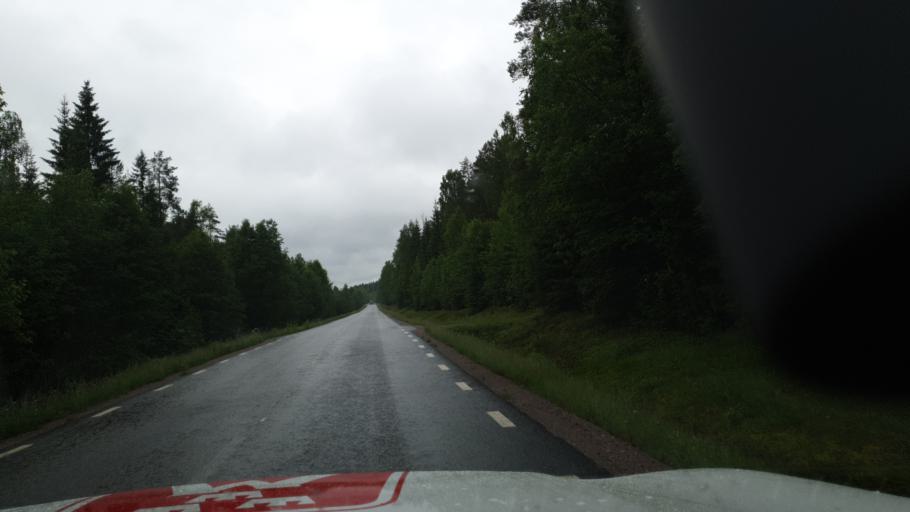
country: SE
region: Vaesterbotten
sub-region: Vannas Kommun
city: Vannasby
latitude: 63.8228
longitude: 19.8563
